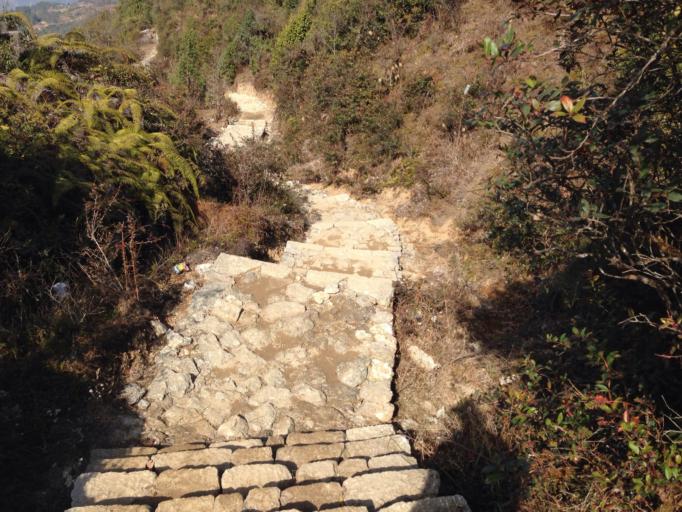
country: NP
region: Central Region
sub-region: Bagmati Zone
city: Nagarkot
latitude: 27.8180
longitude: 85.4476
